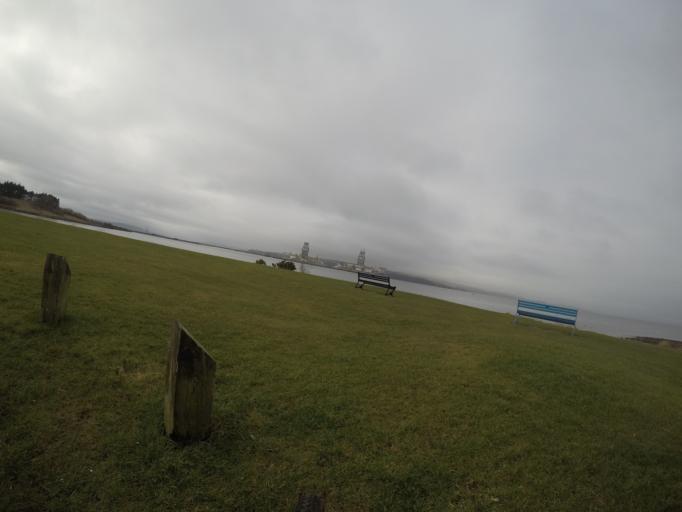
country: GB
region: Scotland
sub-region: North Ayrshire
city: Fairlie
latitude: 55.7515
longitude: -4.8587
